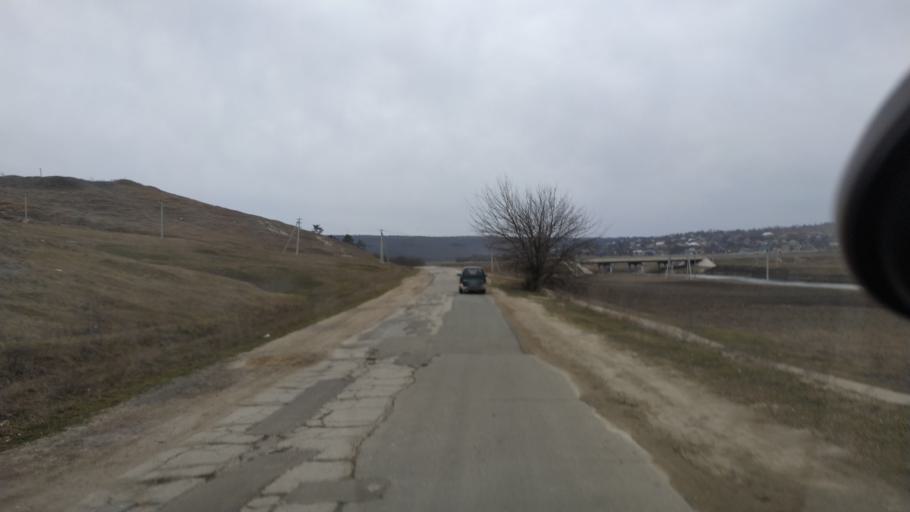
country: MD
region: Telenesti
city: Cocieri
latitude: 47.2608
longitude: 29.0580
